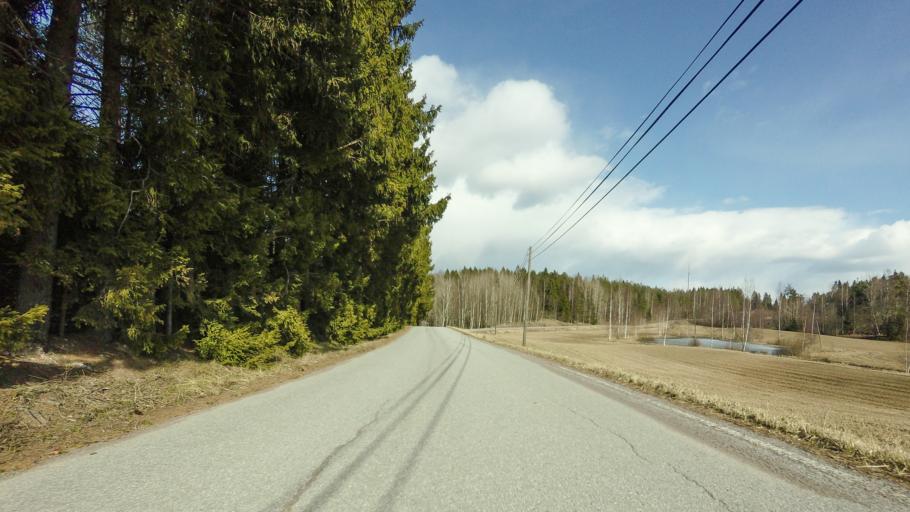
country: FI
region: Uusimaa
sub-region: Helsinki
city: Karjalohja
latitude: 60.2638
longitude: 23.6837
